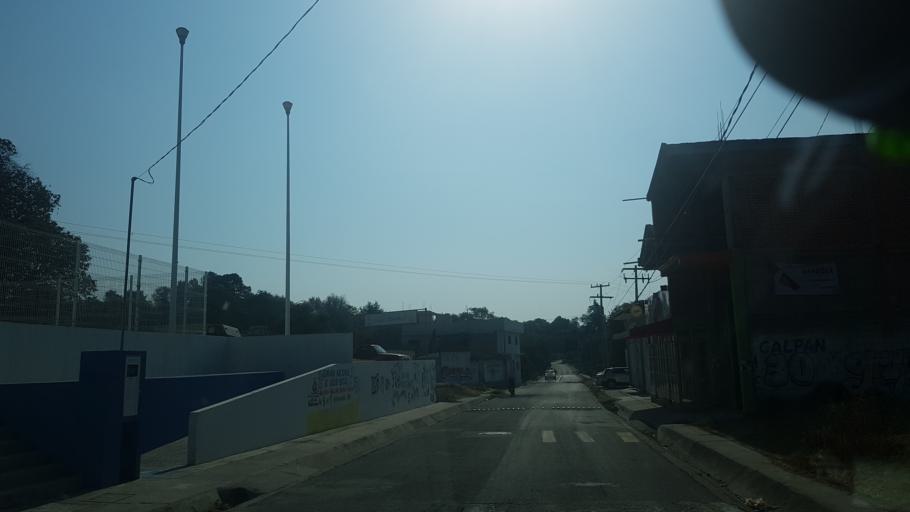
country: MX
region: Puebla
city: San Nicolas de los Ranchos
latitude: 19.0722
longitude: -98.4804
